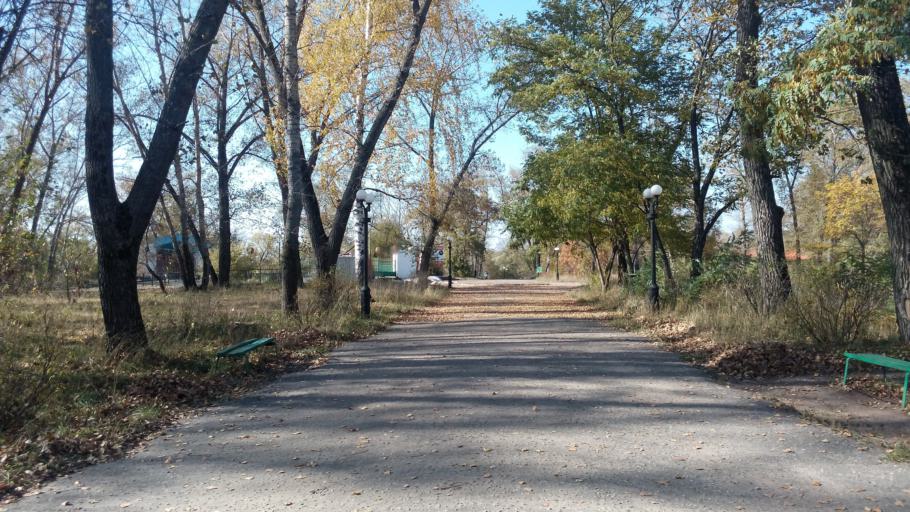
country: RU
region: Tambov
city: Kotovsk
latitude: 52.5861
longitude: 41.4927
